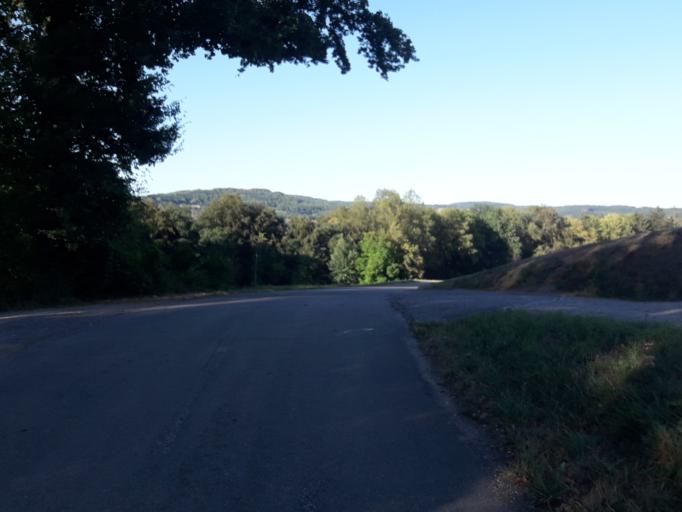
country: CH
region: Aargau
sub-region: Bezirk Baden
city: Unterehrendingen
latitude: 47.5646
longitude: 8.3610
